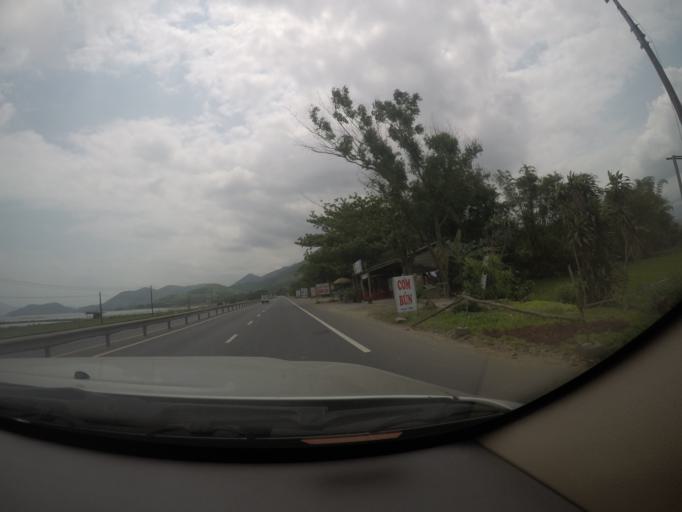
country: VN
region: Thua Thien-Hue
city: Phu Loc
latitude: 16.2930
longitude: 107.8130
